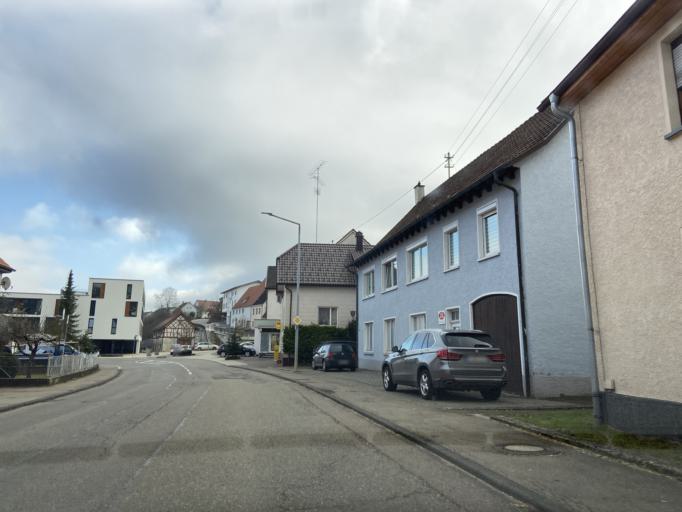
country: DE
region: Baden-Wuerttemberg
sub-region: Tuebingen Region
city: Gammertingen
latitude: 48.2487
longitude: 9.2123
